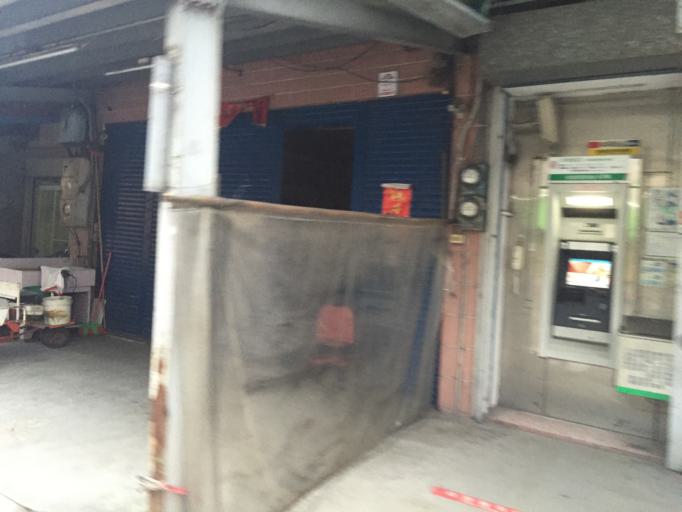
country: TW
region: Taiwan
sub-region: Yilan
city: Yilan
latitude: 24.7796
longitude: 121.7407
